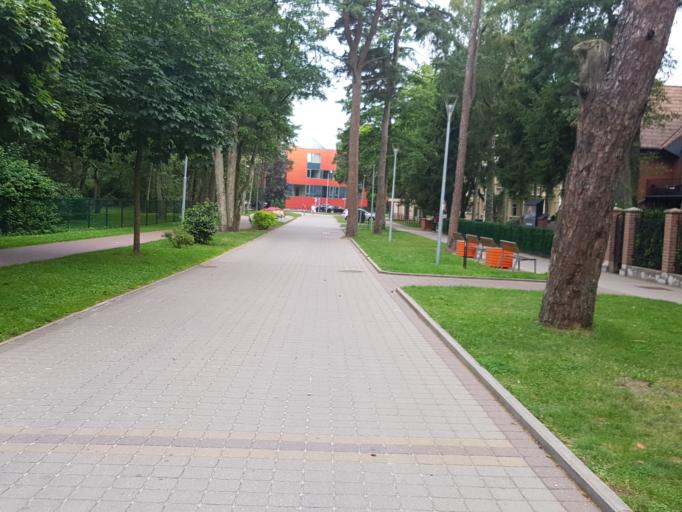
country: LT
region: Klaipedos apskritis
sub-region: Klaipeda
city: Palanga
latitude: 55.9125
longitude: 21.0547
